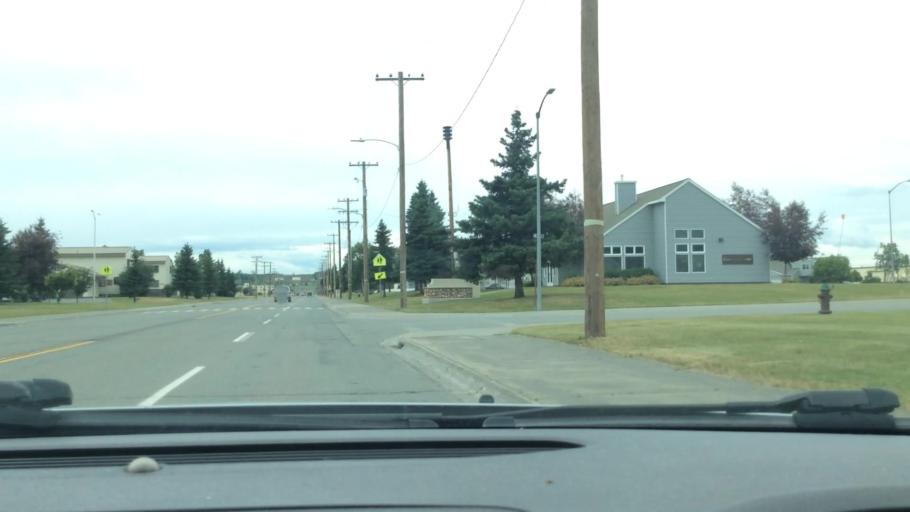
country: US
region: Alaska
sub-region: Anchorage Municipality
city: Anchorage
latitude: 61.2325
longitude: -149.8491
